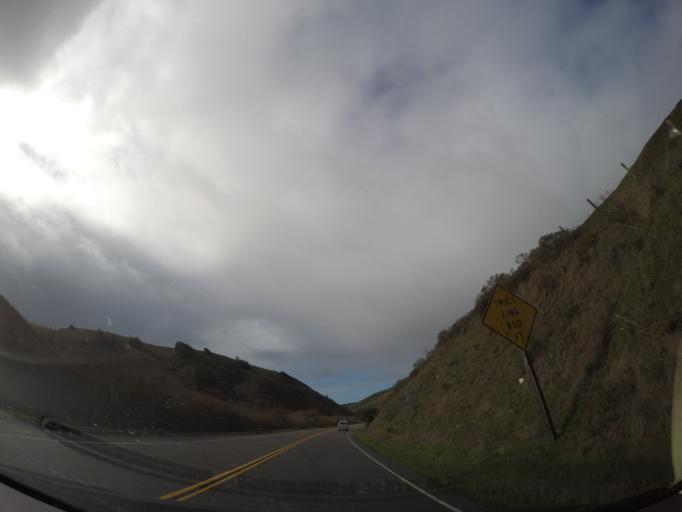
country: US
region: California
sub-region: Sonoma County
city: Bodega Bay
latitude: 38.3271
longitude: -123.0018
